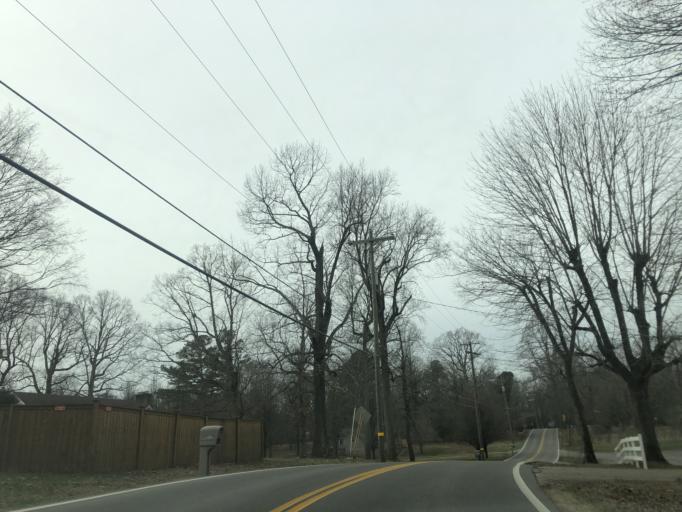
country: US
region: Tennessee
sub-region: Robertson County
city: Ridgetop
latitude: 36.3961
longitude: -86.7761
